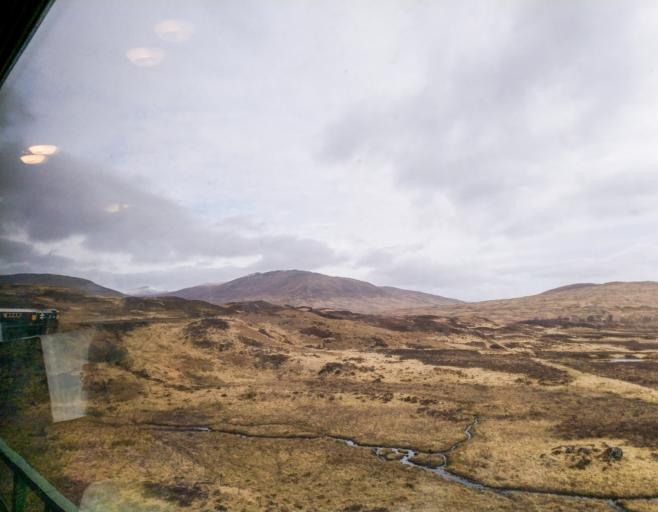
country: GB
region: Scotland
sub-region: Highland
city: Spean Bridge
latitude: 56.6895
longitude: -4.5767
